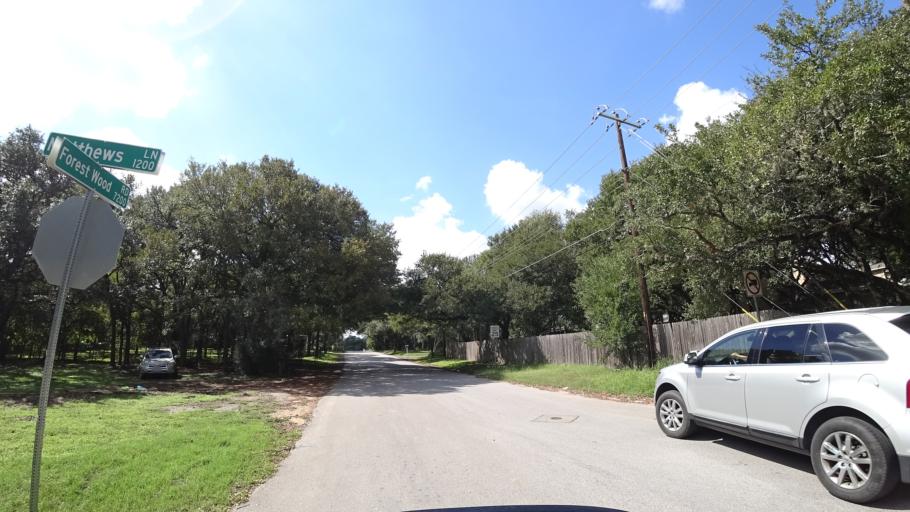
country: US
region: Texas
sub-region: Travis County
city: Onion Creek
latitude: 30.1965
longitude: -97.8003
